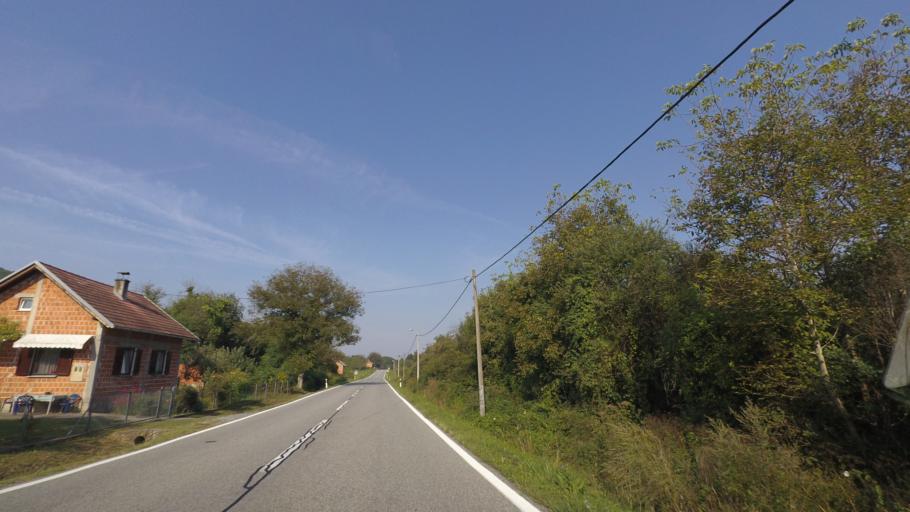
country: HR
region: Bjelovarsko-Bilogorska
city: Sirac
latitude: 45.4678
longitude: 17.3878
